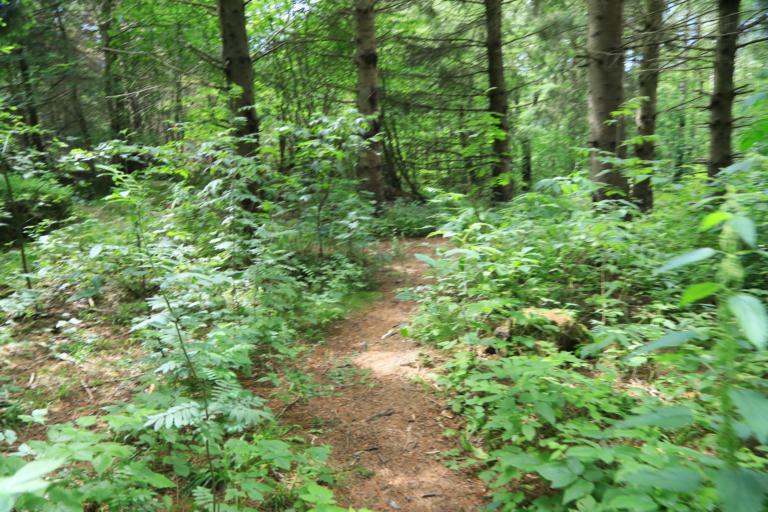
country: SE
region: Halland
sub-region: Varbergs Kommun
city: Varberg
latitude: 57.1198
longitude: 12.2667
